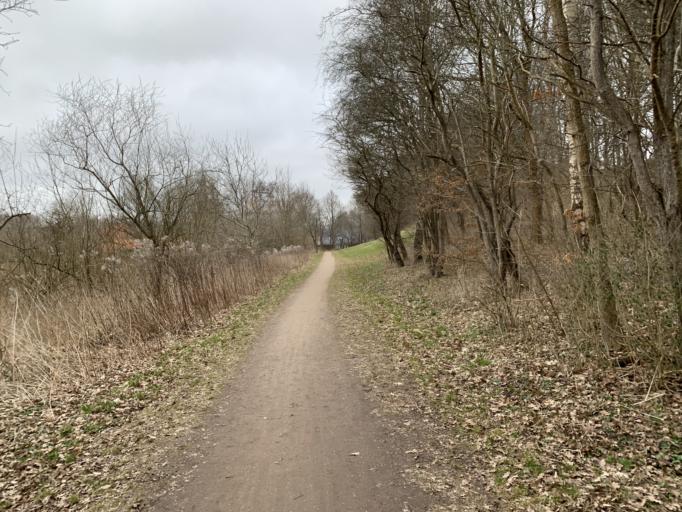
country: DK
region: South Denmark
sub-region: Odense Kommune
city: Odense
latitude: 55.4143
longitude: 10.3127
